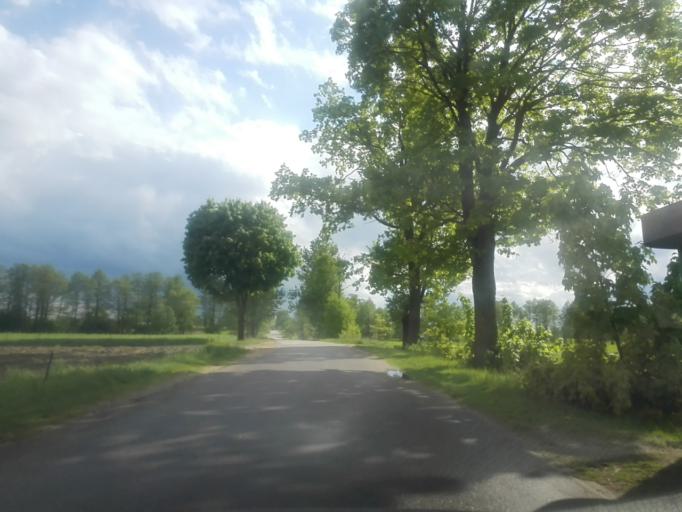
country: PL
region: Podlasie
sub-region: Powiat lomzynski
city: Wizna
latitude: 53.2304
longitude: 22.4232
